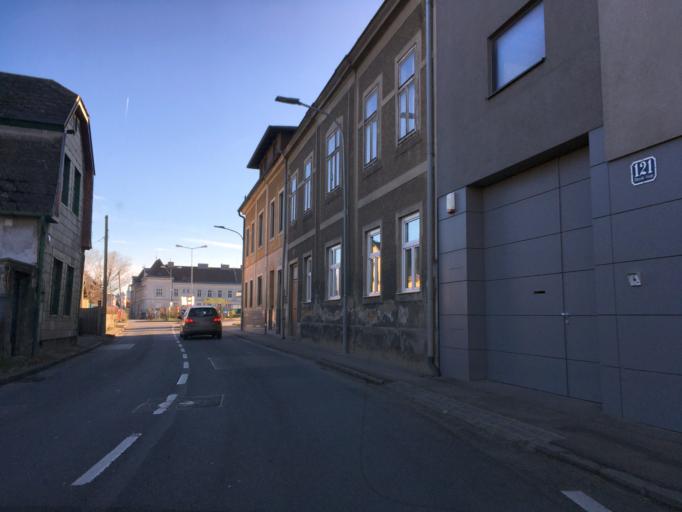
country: AT
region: Lower Austria
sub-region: Politischer Bezirk Wien-Umgebung
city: Klosterneuburg
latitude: 48.3164
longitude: 16.3137
